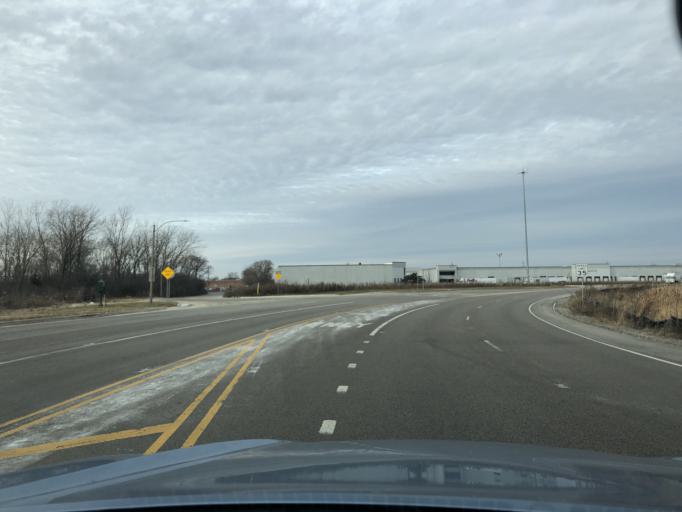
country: US
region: Illinois
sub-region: DuPage County
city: Bensenville
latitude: 41.9761
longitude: -87.9401
